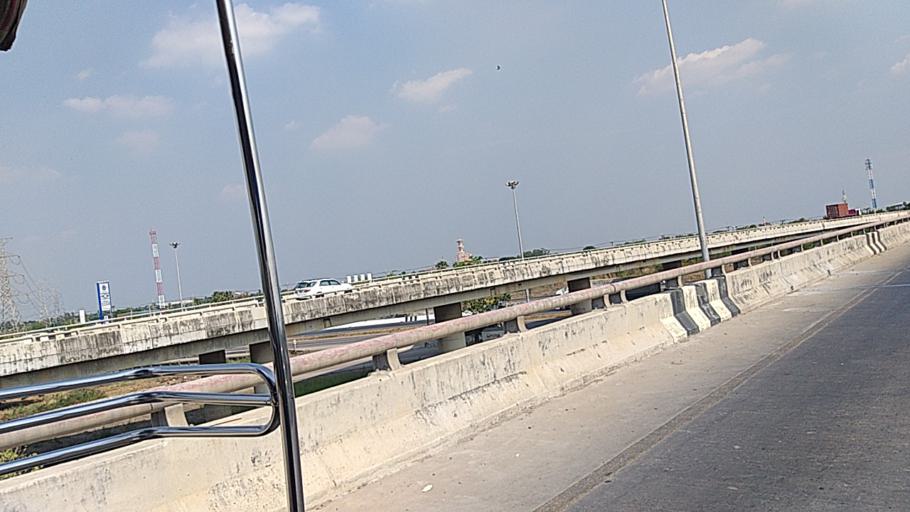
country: TH
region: Pathum Thani
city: Sam Khok
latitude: 14.0940
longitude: 100.5182
